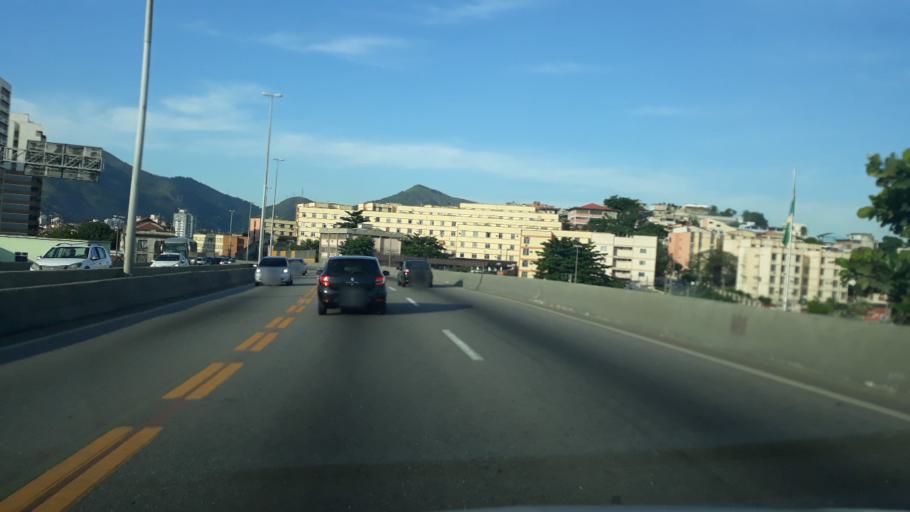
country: BR
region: Rio de Janeiro
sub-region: Rio De Janeiro
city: Rio de Janeiro
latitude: -22.8837
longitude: -43.2898
